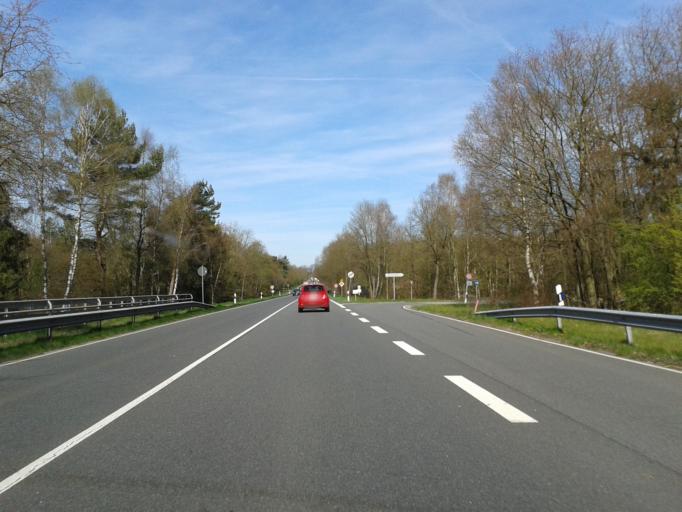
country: DE
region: Lower Saxony
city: Munster
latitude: 52.9752
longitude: 10.1018
